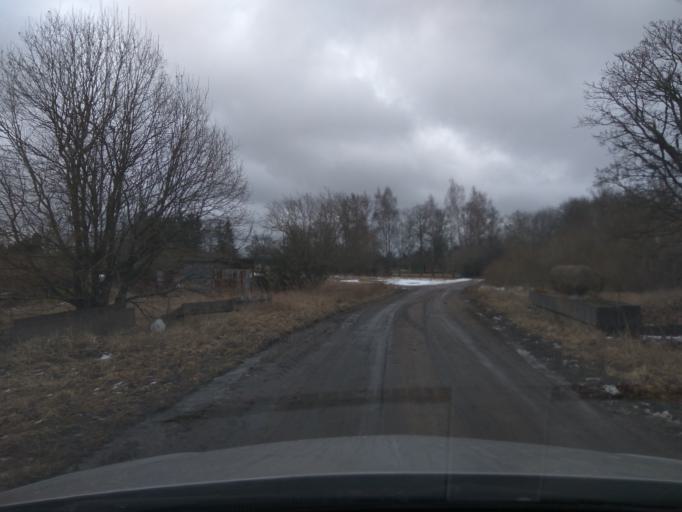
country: LV
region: Ventspils
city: Ventspils
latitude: 57.3339
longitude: 21.6454
